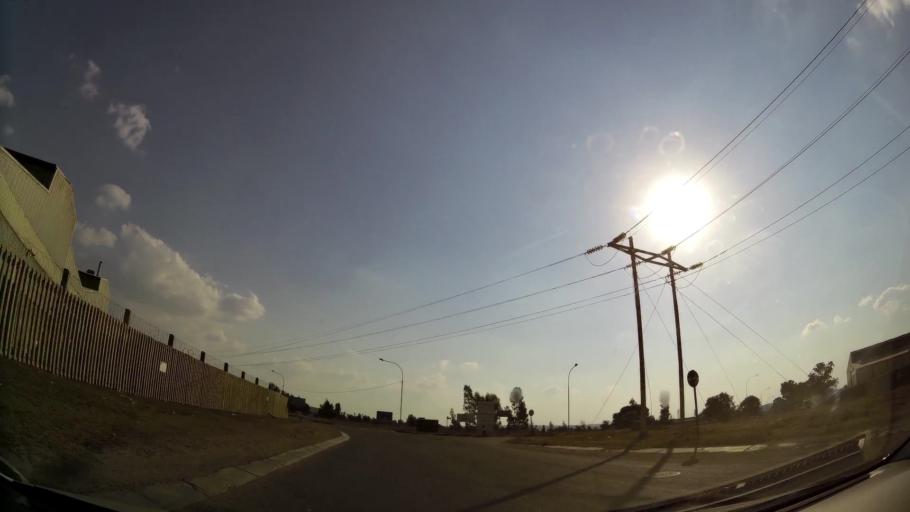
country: ZA
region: Gauteng
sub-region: Ekurhuleni Metropolitan Municipality
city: Tembisa
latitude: -25.9459
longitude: 28.2251
